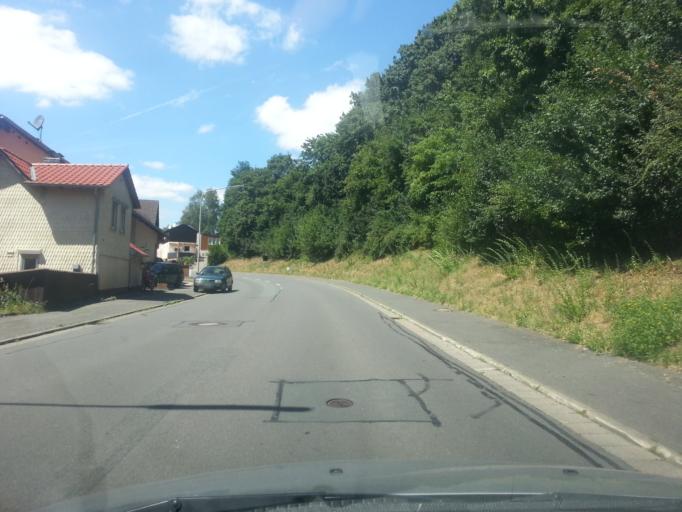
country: DE
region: Hesse
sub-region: Regierungsbezirk Darmstadt
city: Bad Konig
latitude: 49.7264
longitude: 8.9717
